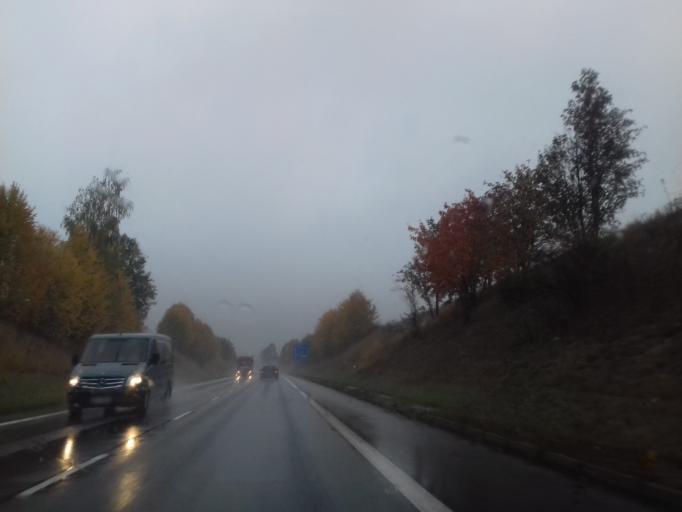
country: CZ
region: Kralovehradecky
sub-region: Okres Jicin
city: Jicin
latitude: 50.4383
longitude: 15.3385
